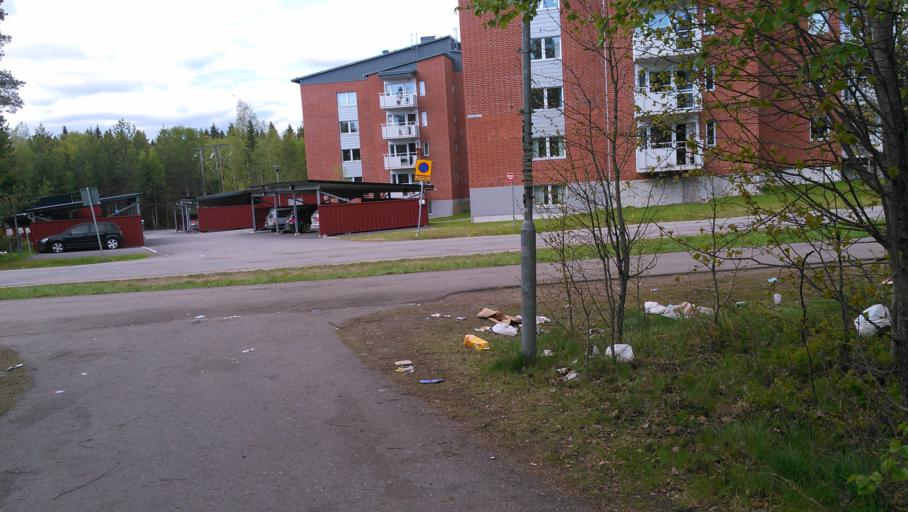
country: SE
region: Vaesterbotten
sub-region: Umea Kommun
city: Ersmark
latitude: 63.8249
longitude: 20.3270
